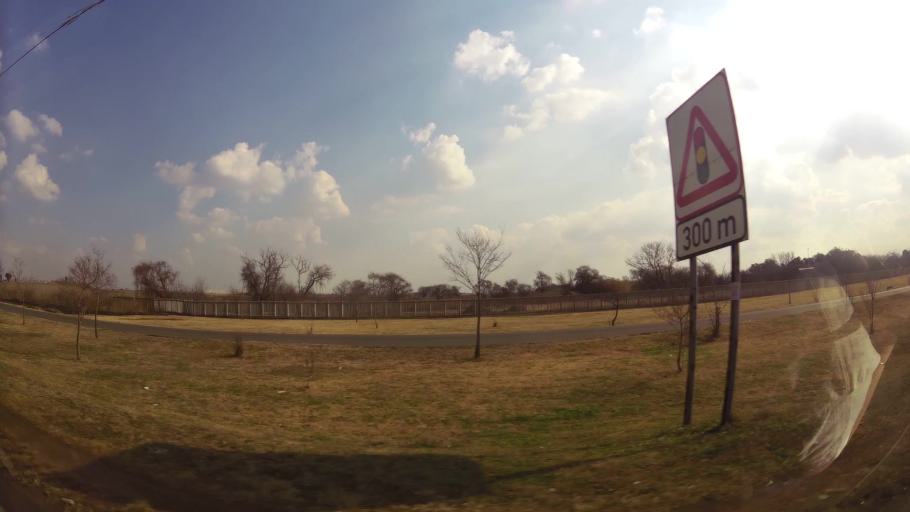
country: ZA
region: Gauteng
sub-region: Ekurhuleni Metropolitan Municipality
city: Germiston
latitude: -26.2972
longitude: 28.2133
